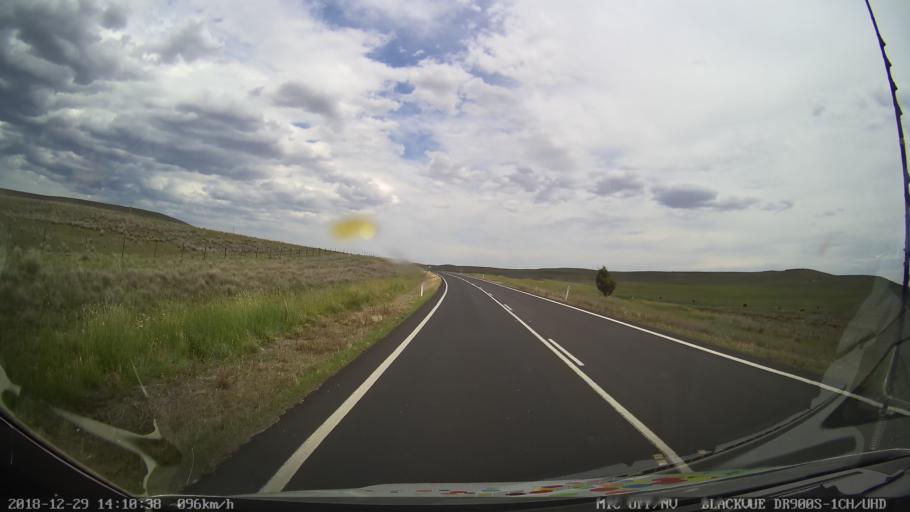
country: AU
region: New South Wales
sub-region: Cooma-Monaro
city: Cooma
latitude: -36.3945
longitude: 149.2167
